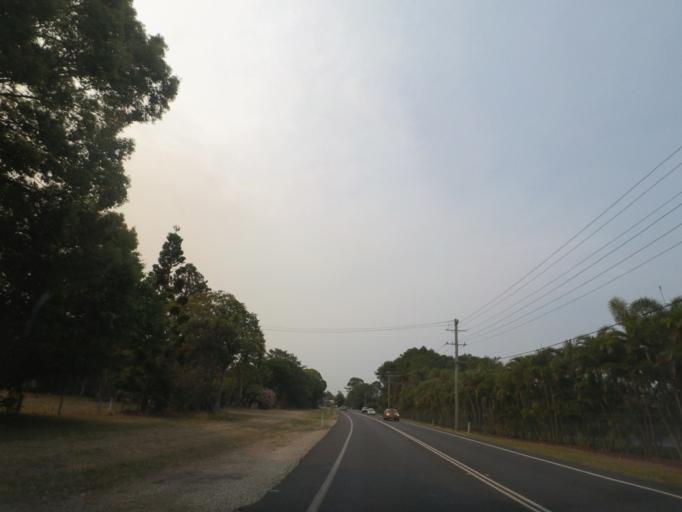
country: AU
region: New South Wales
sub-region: Tweed
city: Kingscliff
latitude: -28.2548
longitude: 153.5596
